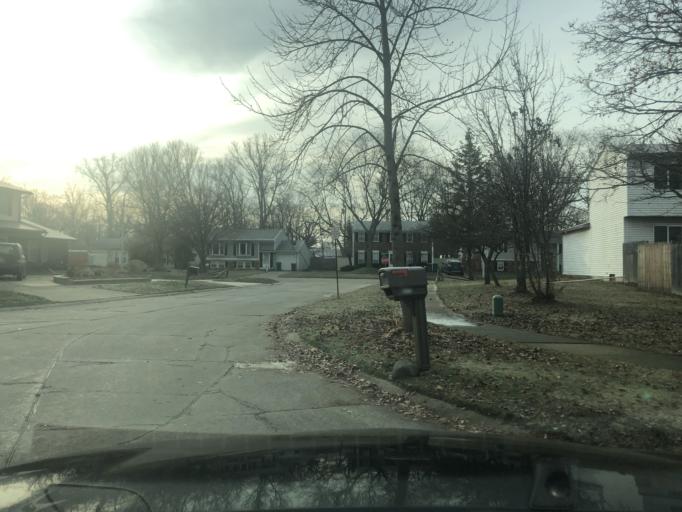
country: US
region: Michigan
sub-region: Wayne County
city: Taylor
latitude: 42.1856
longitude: -83.3249
